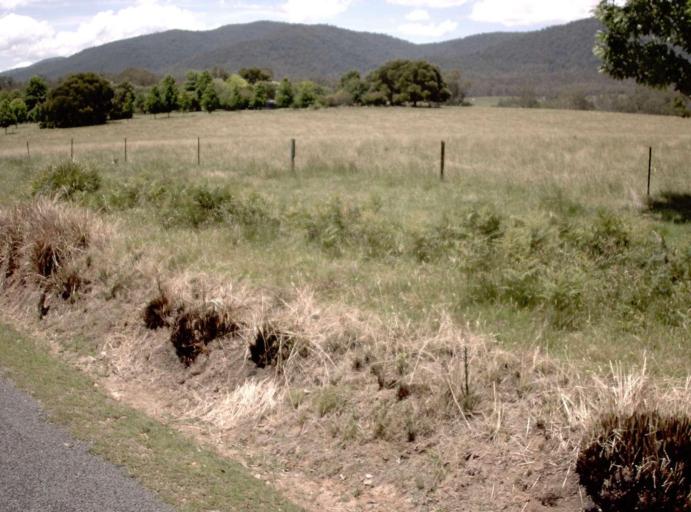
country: AU
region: New South Wales
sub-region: Bombala
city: Bombala
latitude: -37.4174
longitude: 149.0097
